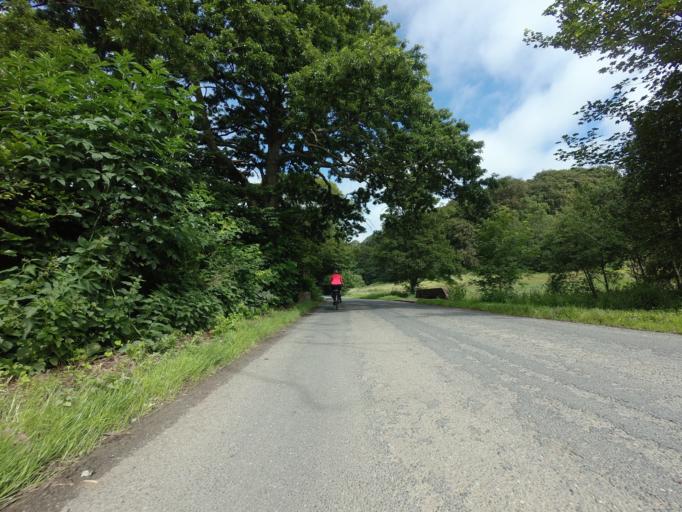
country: GB
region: Scotland
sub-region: Aberdeenshire
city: Turriff
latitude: 57.5486
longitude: -2.4830
